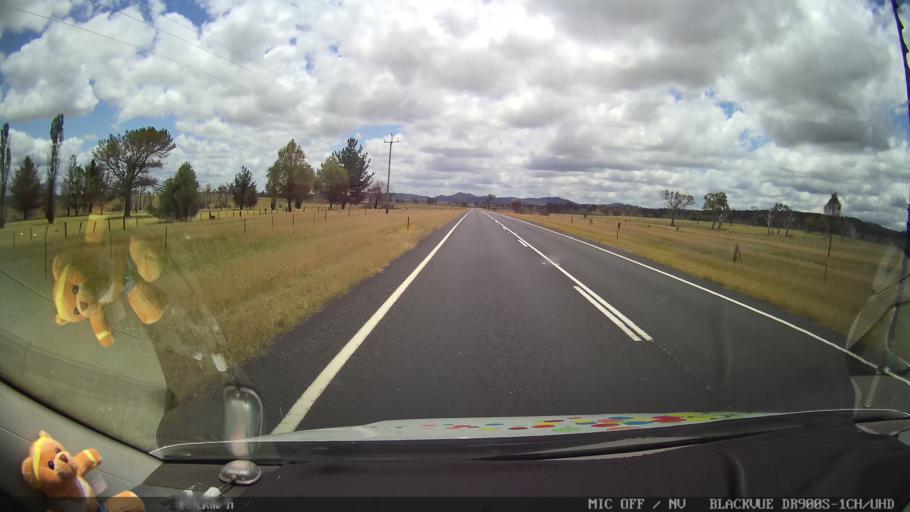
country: AU
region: New South Wales
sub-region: Glen Innes Severn
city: Glen Innes
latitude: -29.4279
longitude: 151.8569
